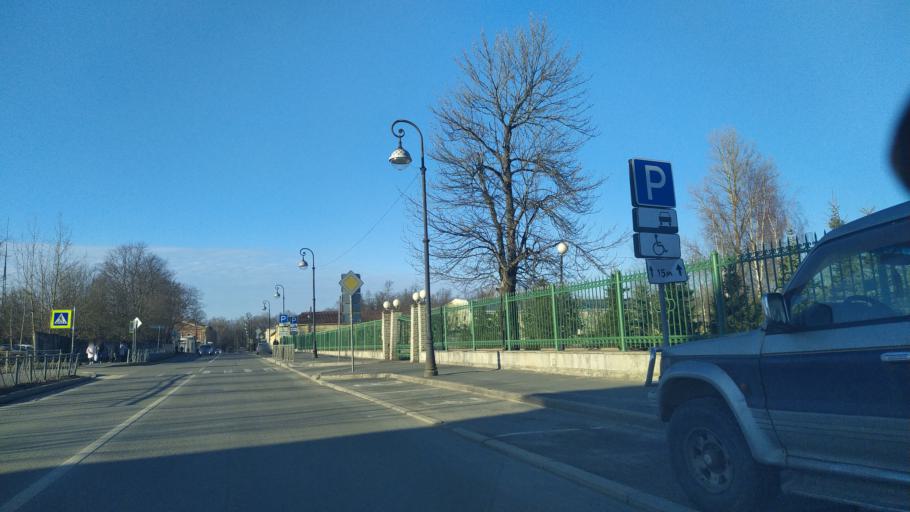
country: RU
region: St.-Petersburg
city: Pushkin
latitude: 59.7049
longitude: 30.3919
